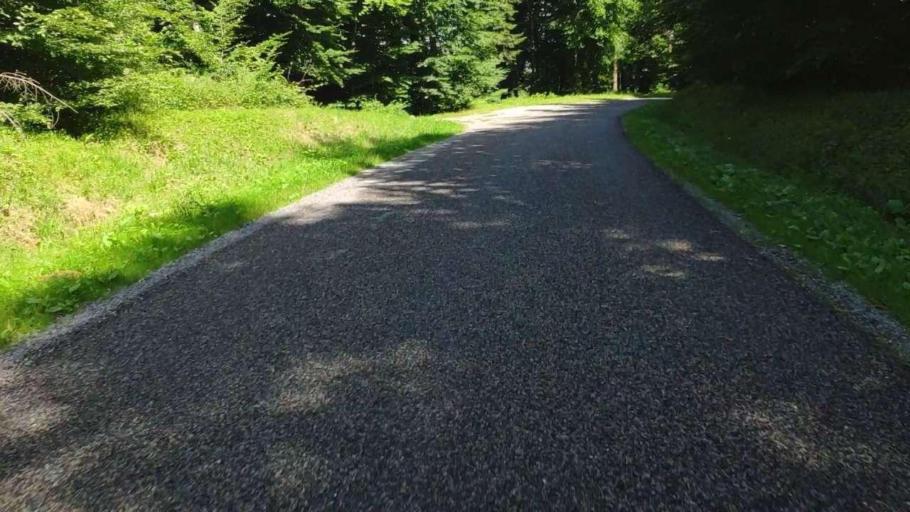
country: FR
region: Franche-Comte
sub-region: Departement du Jura
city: Bletterans
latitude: 46.8068
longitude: 5.5612
